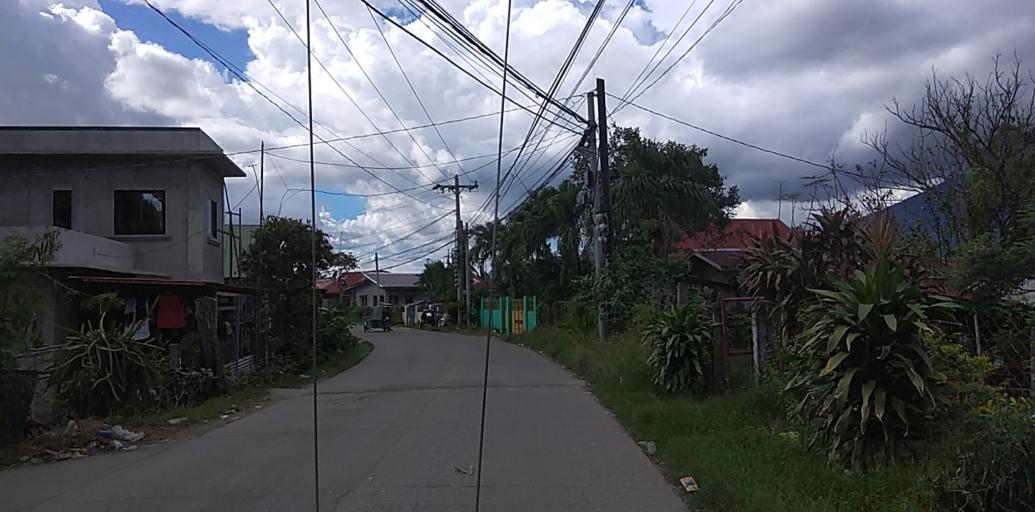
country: PH
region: Central Luzon
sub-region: Province of Pampanga
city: Arayat
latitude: 15.1397
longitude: 120.7746
